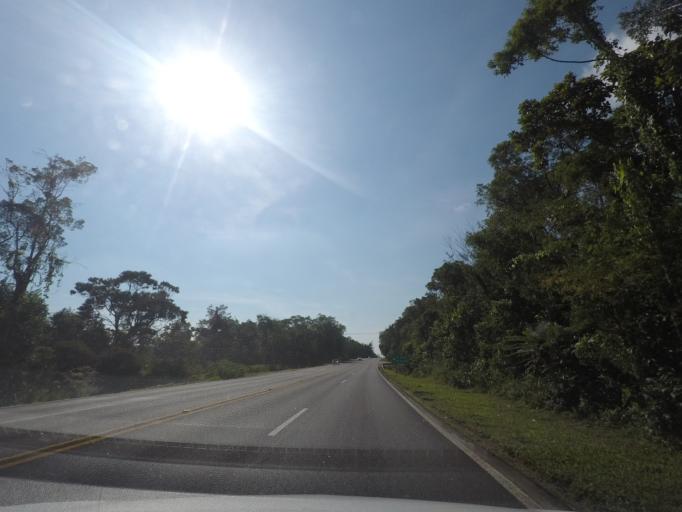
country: BR
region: Parana
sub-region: Paranagua
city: Paranagua
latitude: -25.5981
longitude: -48.6104
